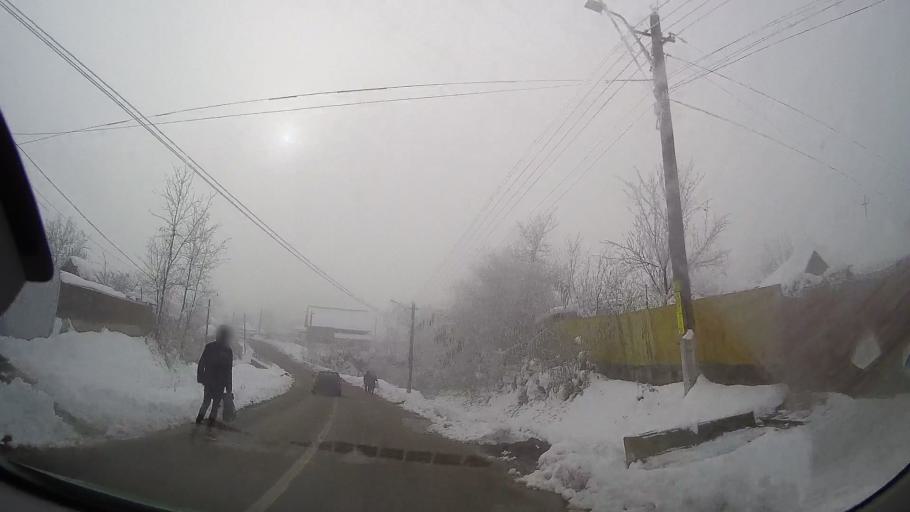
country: RO
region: Iasi
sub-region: Comuna Valea Seaca
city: Valea Seaca
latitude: 47.2902
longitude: 26.6666
